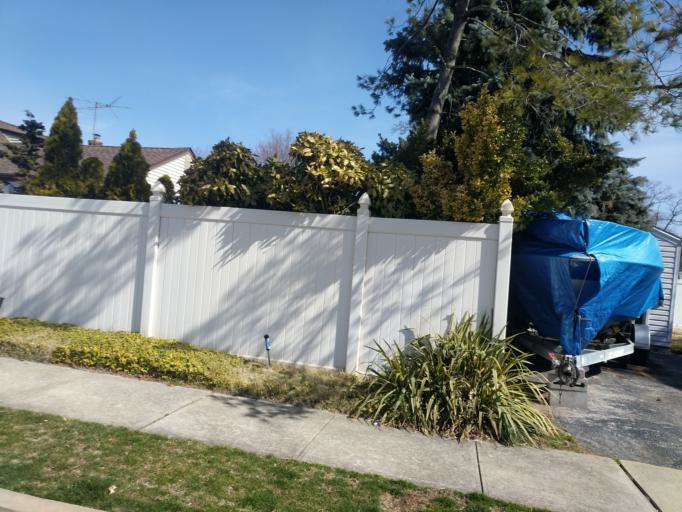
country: US
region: New York
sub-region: Nassau County
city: Hewlett
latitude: 40.6539
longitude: -73.6910
